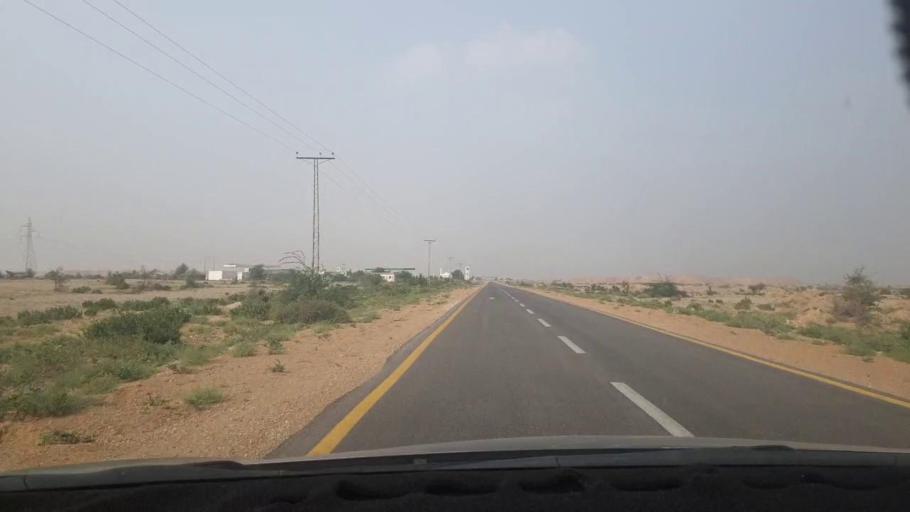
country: PK
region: Sindh
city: Jamshoro
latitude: 25.5681
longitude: 68.3163
